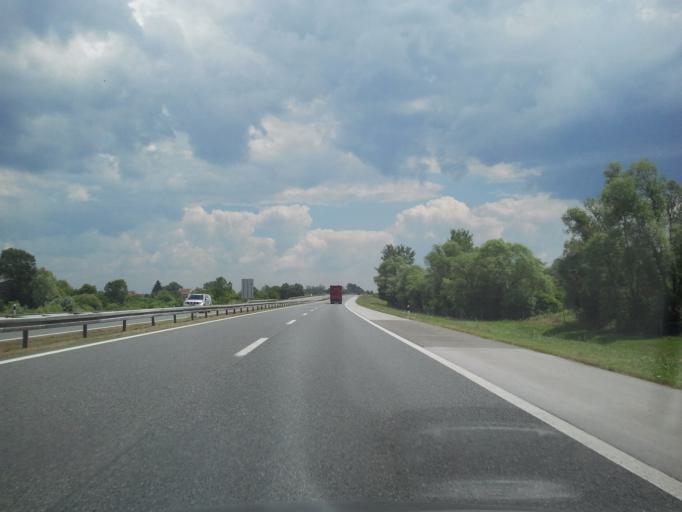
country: HR
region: Sisacko-Moslavacka
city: Novska
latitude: 45.3258
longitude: 16.9587
